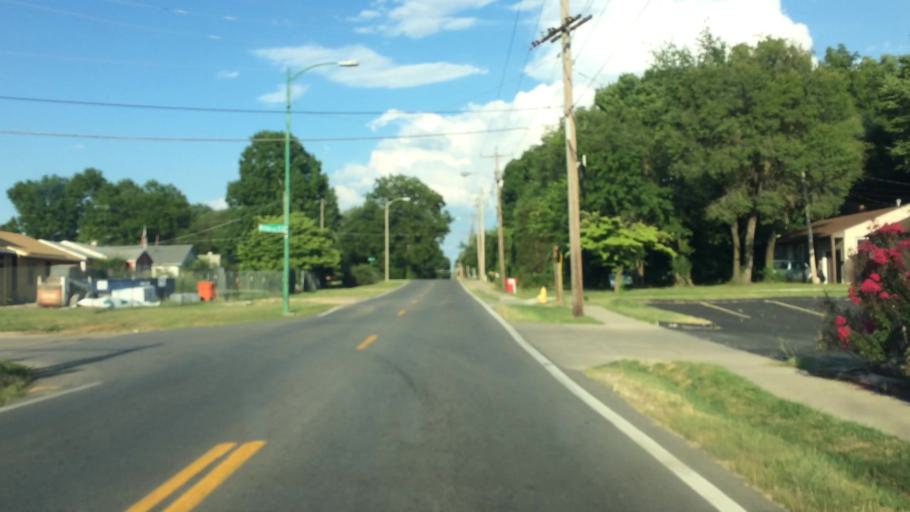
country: US
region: Missouri
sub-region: Greene County
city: Springfield
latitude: 37.1961
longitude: -93.2576
